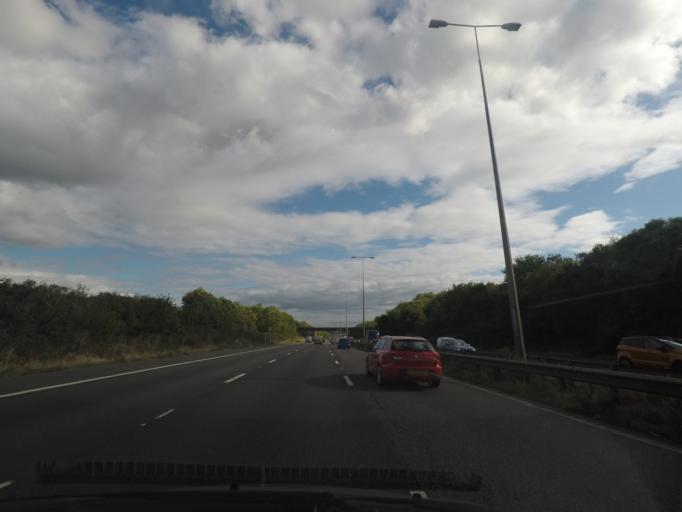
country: GB
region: England
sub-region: Leicestershire
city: Shepshed
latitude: 52.7929
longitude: -1.2913
